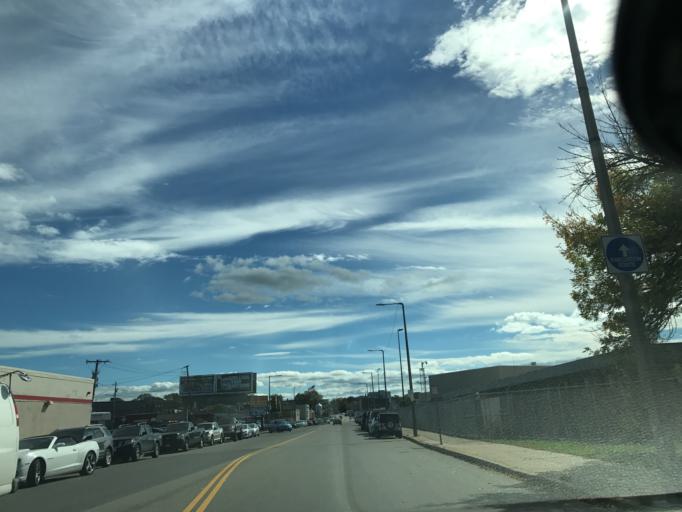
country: US
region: Massachusetts
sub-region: Suffolk County
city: South Boston
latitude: 42.3243
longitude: -71.0648
